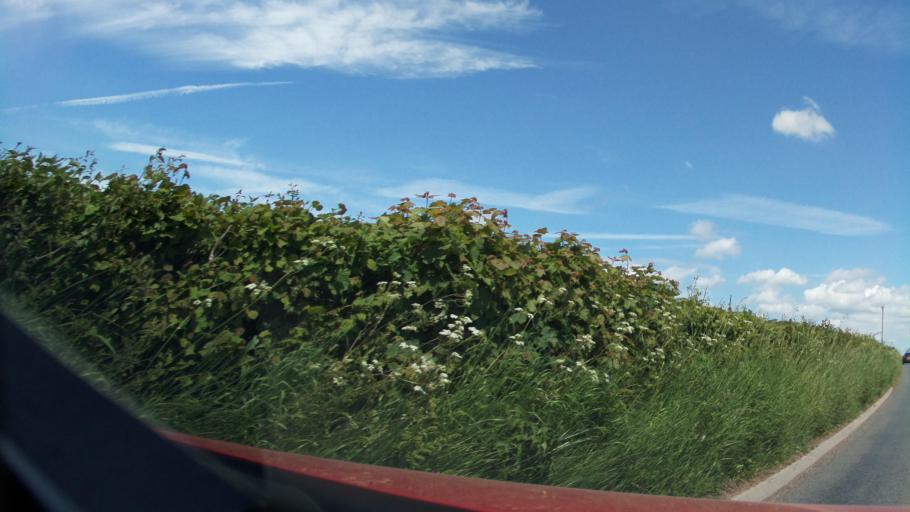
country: GB
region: Wales
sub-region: Monmouthshire
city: Mitchel Troy
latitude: 51.7290
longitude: -2.7527
